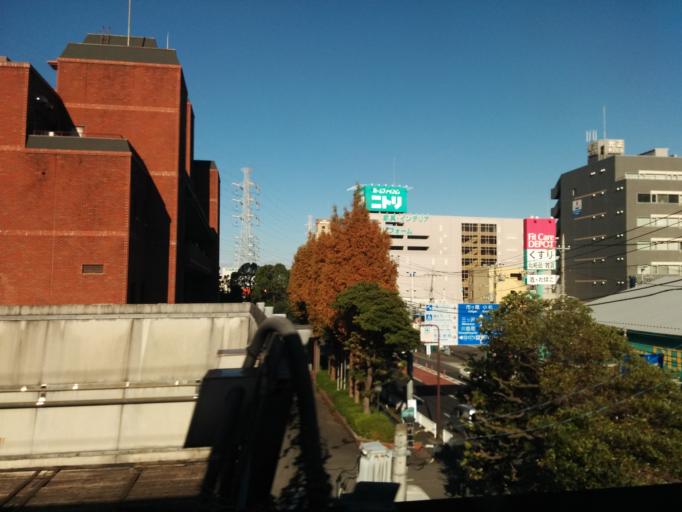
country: JP
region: Kanagawa
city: Yokohama
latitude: 35.5010
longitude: 139.6095
